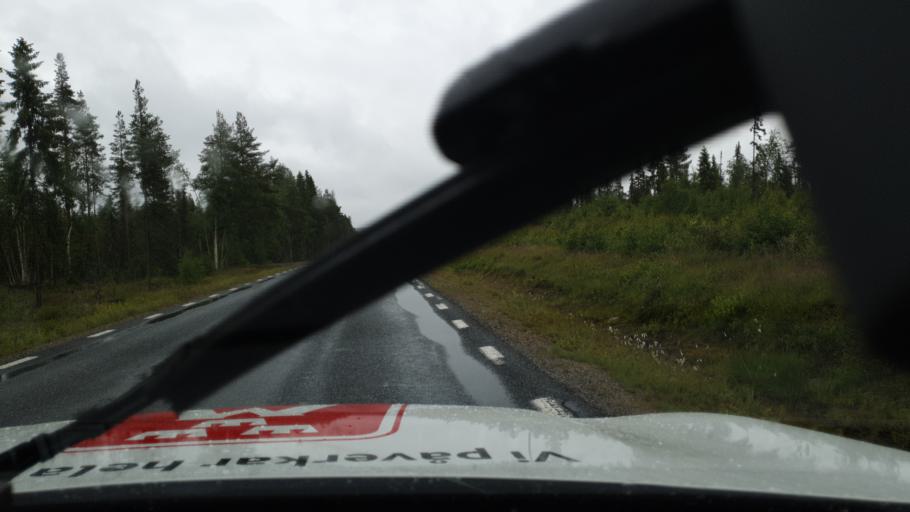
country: SE
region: Vaesterbotten
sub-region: Asele Kommun
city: Insjon
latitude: 64.2935
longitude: 17.6646
